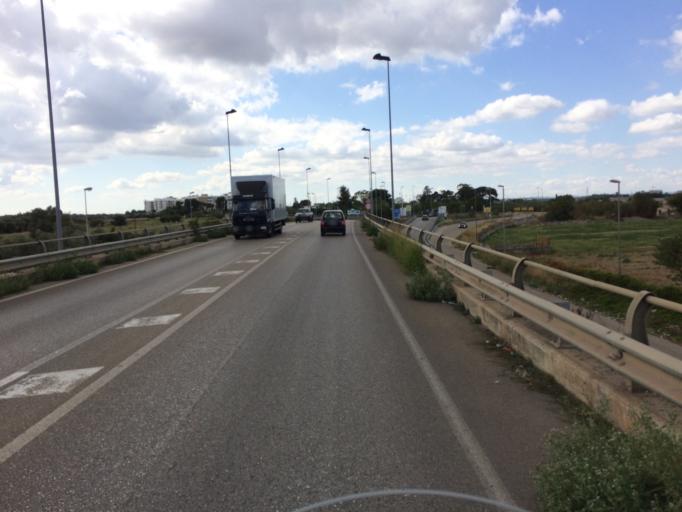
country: IT
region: Apulia
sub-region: Provincia di Bari
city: Bari
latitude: 41.0962
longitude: 16.8293
